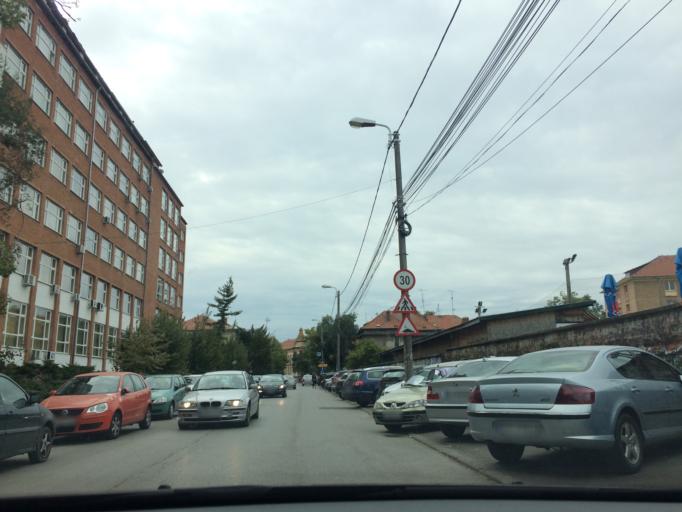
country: RO
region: Timis
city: Timisoara
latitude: 45.7462
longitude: 21.2295
